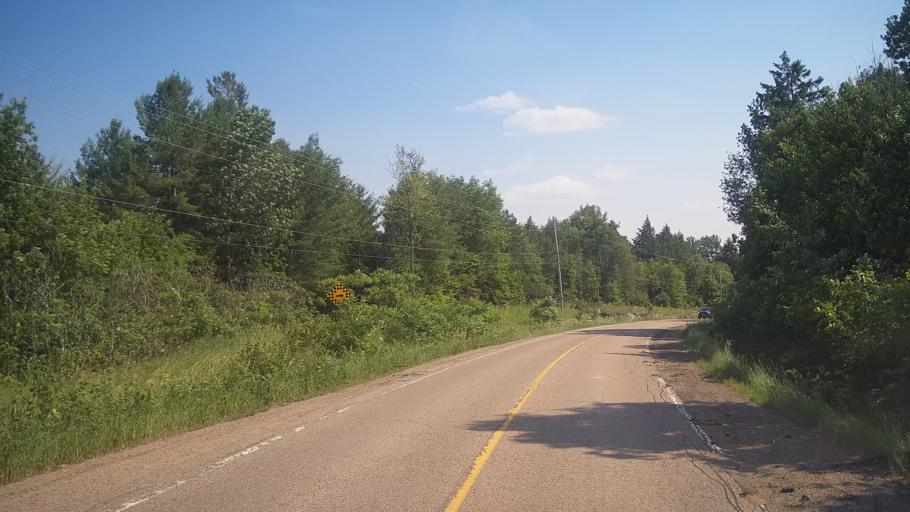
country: CA
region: Ontario
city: Pembroke
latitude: 45.5881
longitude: -77.2265
